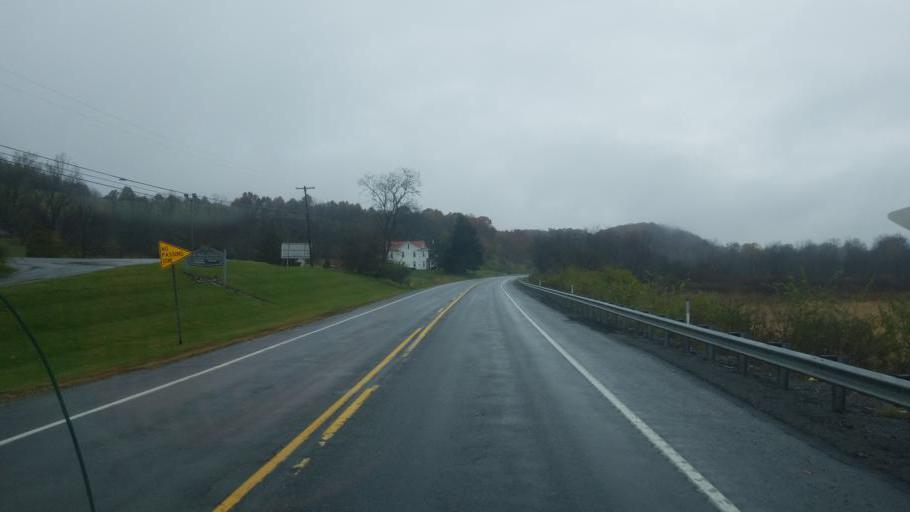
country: US
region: Pennsylvania
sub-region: Centre County
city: Milesburg
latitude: 40.9720
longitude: -77.7505
